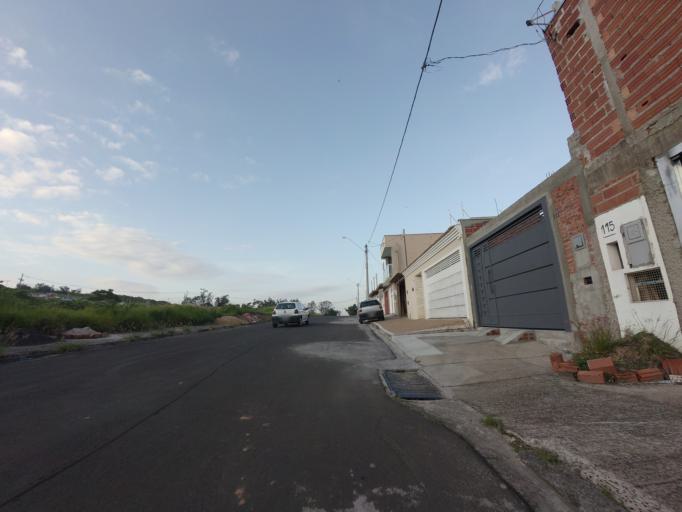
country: BR
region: Sao Paulo
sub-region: Piracicaba
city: Piracicaba
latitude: -22.7630
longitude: -47.6090
